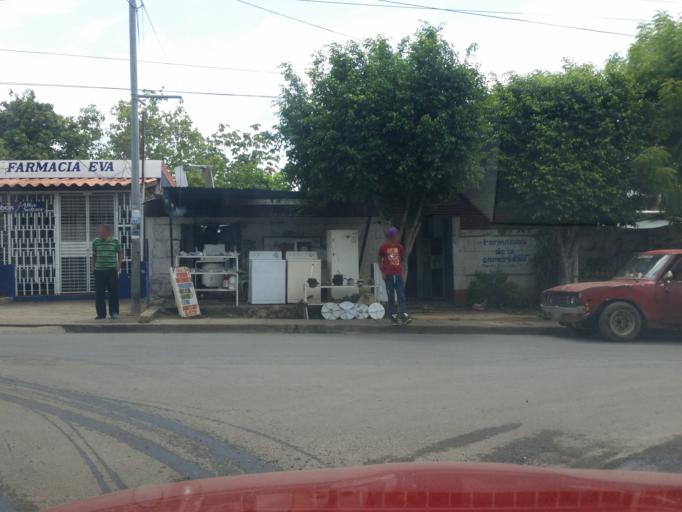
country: NI
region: Managua
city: Managua
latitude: 12.1056
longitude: -86.2333
